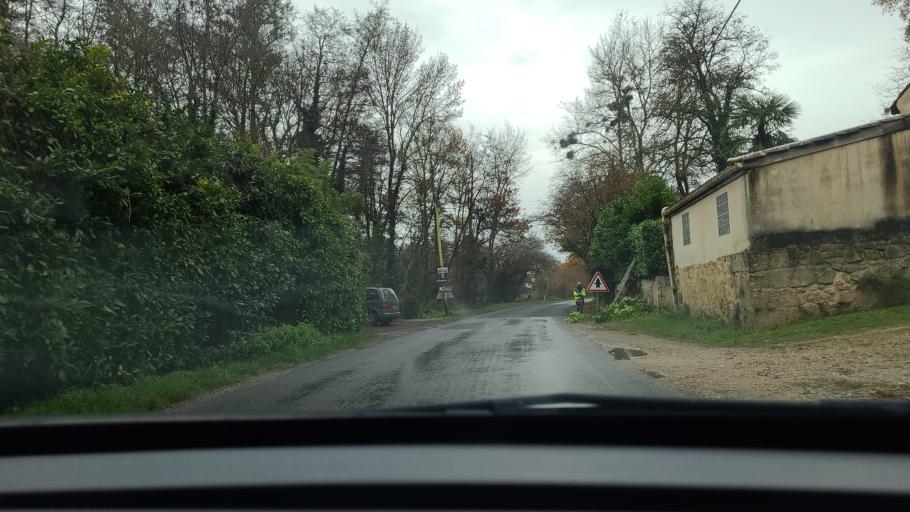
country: FR
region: Aquitaine
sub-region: Departement de la Gironde
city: Tauriac
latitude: 45.0401
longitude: -0.5071
